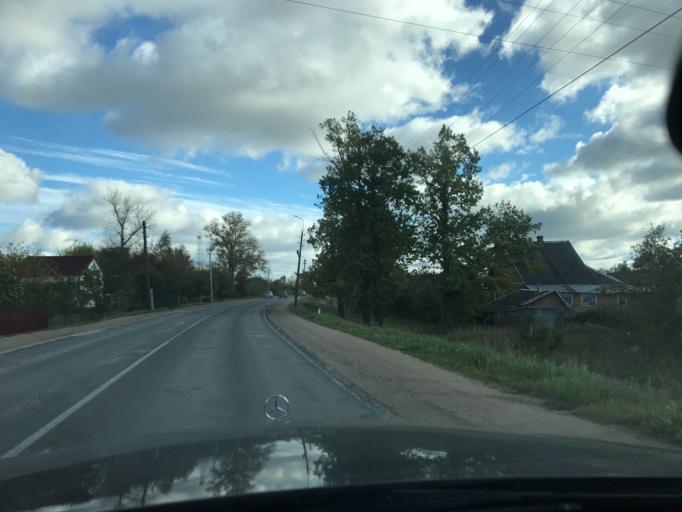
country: RU
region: Pskov
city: Ostrov
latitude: 57.3544
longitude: 28.3310
